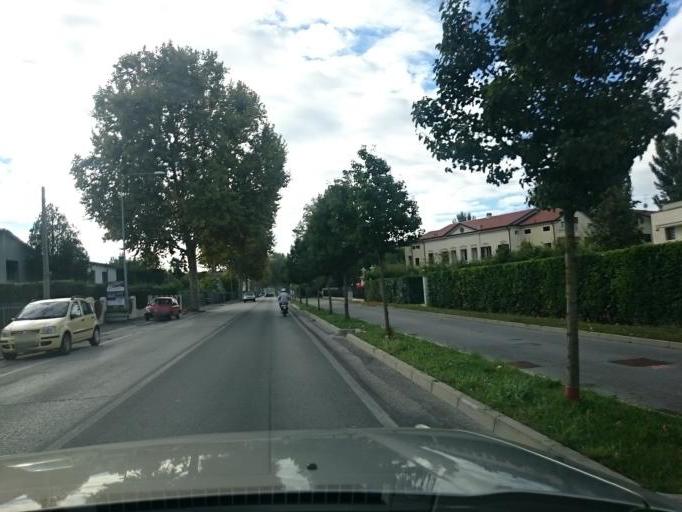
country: IT
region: Veneto
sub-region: Provincia di Padova
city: Albignasego
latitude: 45.3745
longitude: 11.8870
